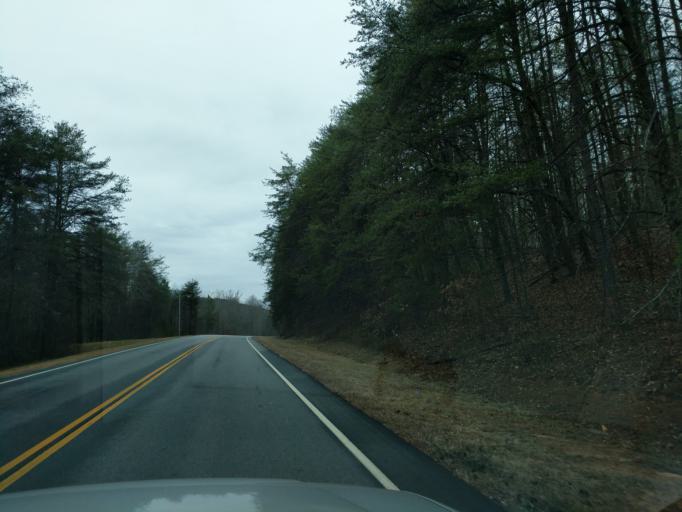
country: US
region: South Carolina
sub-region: Greenville County
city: Slater-Marietta
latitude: 35.0829
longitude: -82.4922
